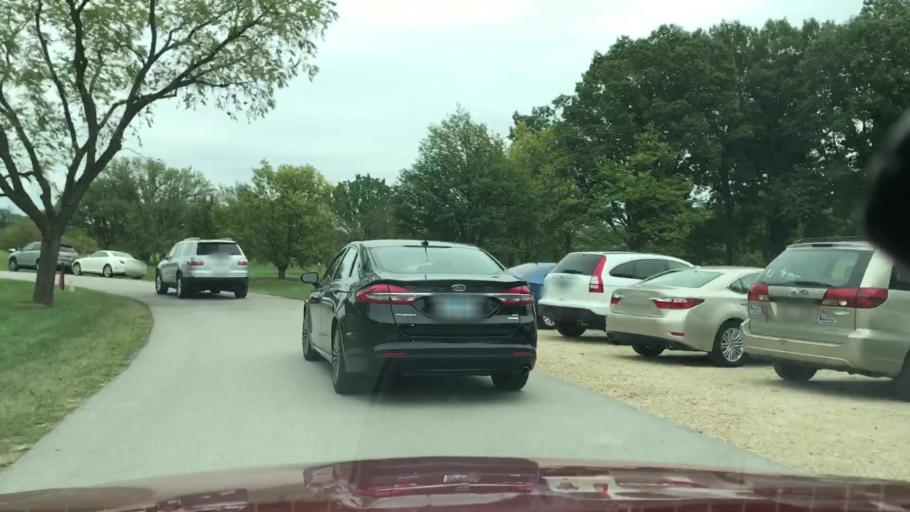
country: US
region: Illinois
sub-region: DuPage County
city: Lisle
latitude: 41.8120
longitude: -88.0639
